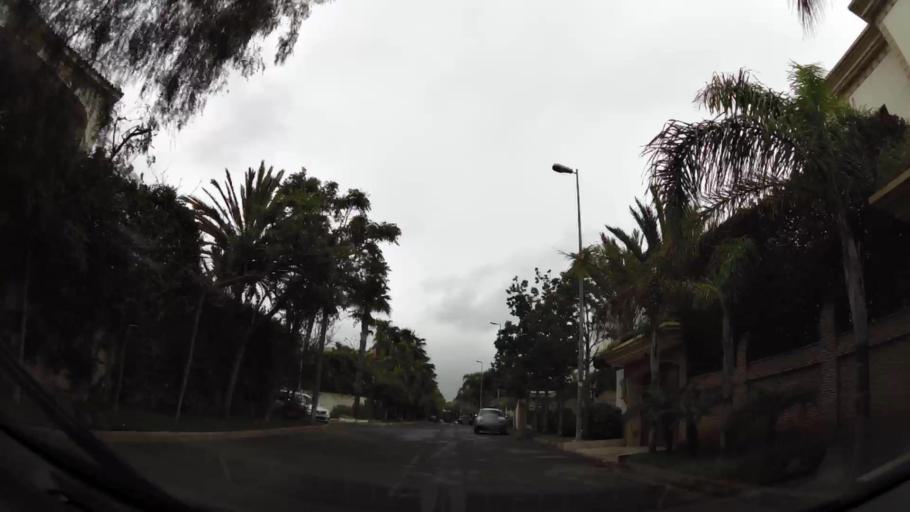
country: MA
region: Grand Casablanca
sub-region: Casablanca
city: Casablanca
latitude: 33.5394
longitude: -7.6300
